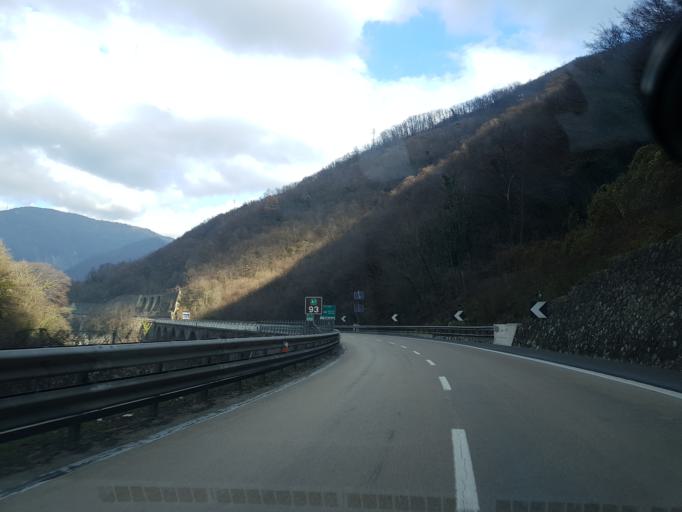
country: IT
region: Liguria
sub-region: Provincia di Genova
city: Isola del Cantone
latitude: 44.6342
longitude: 8.9494
